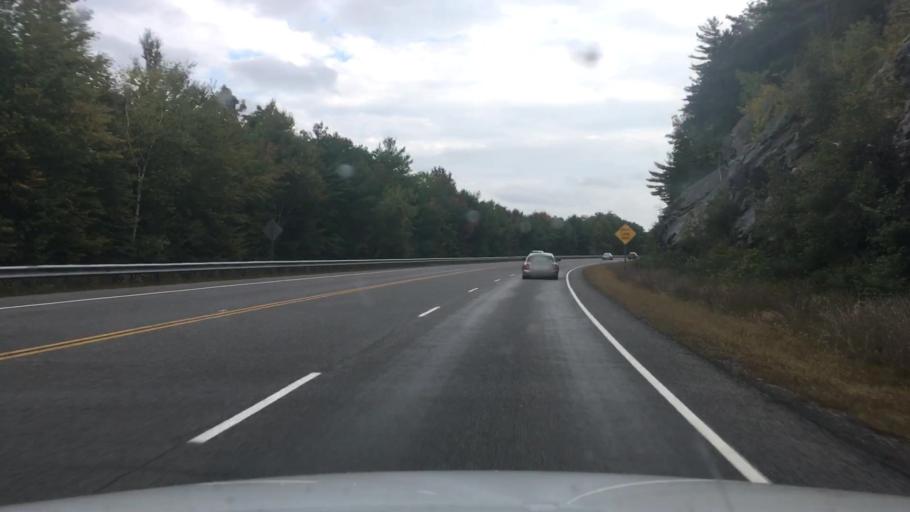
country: US
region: New Hampshire
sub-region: Carroll County
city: Wolfeboro
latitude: 43.5351
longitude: -71.2781
